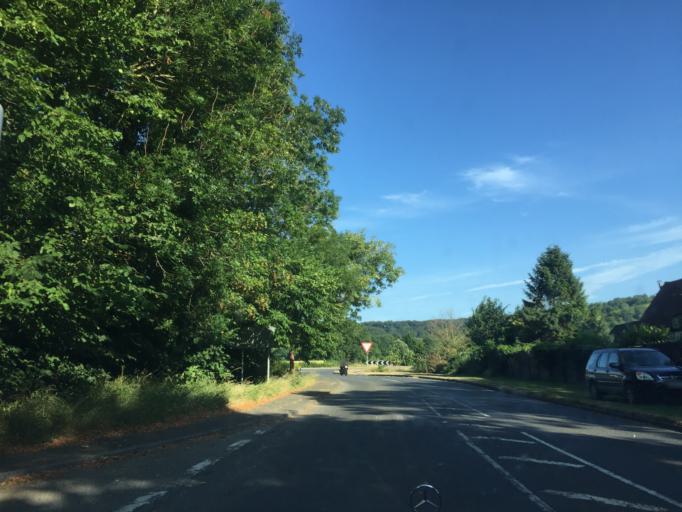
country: GB
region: England
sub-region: Oxfordshire
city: Chinnor
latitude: 51.6774
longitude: -0.9545
